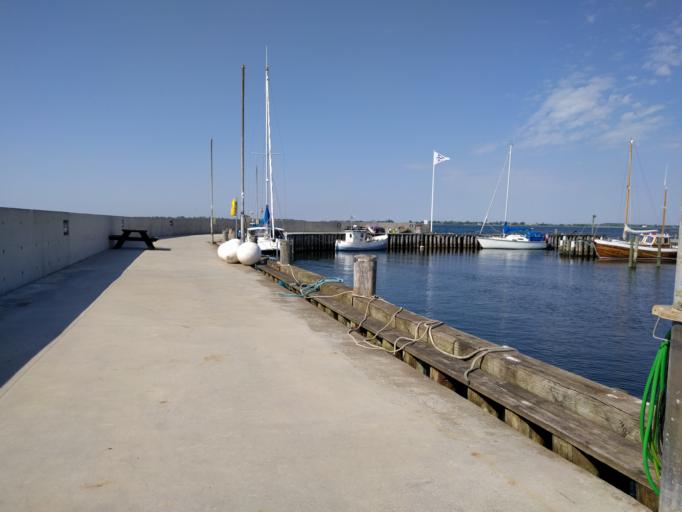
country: DK
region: South Denmark
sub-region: Kerteminde Kommune
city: Munkebo
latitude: 55.4859
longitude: 10.5974
